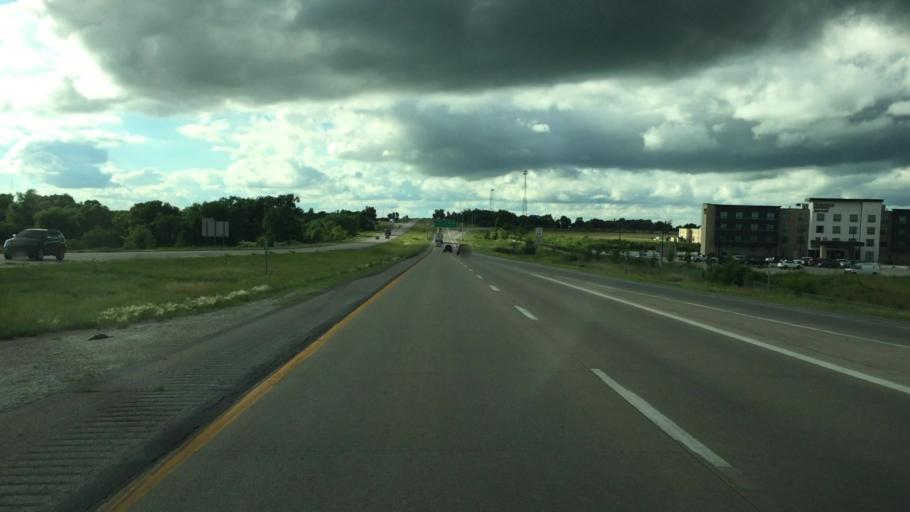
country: US
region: Iowa
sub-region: Polk County
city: Altoona
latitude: 41.6510
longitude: -93.5151
